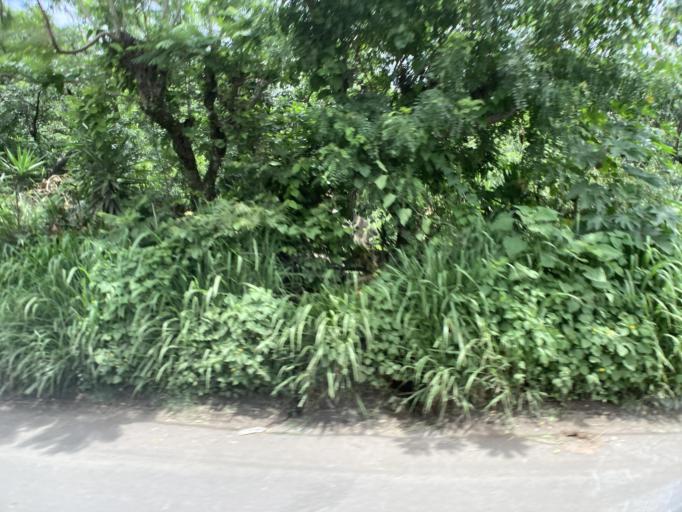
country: GT
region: Guatemala
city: Villa Canales
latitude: 14.4485
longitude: -90.5655
